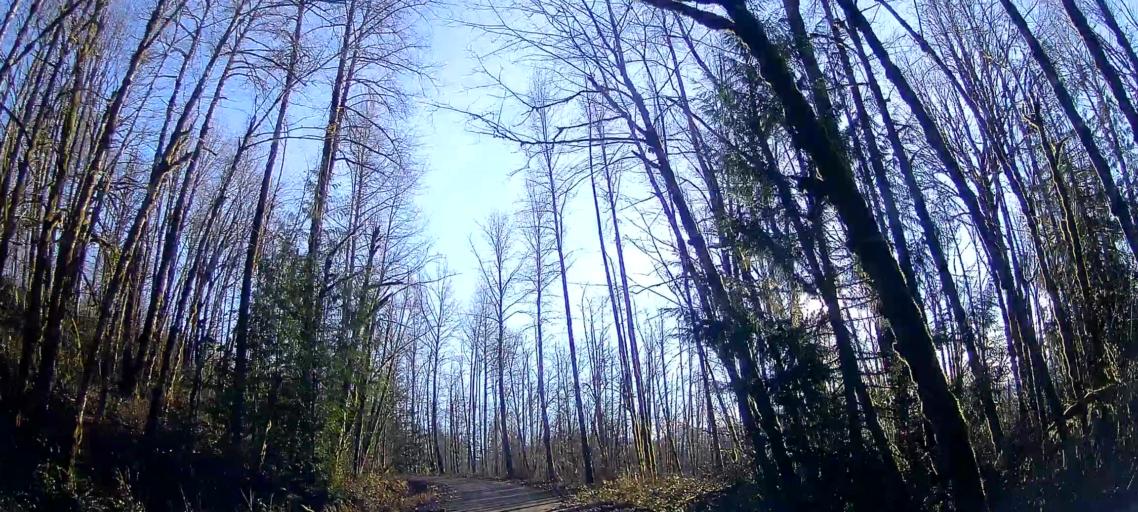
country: US
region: Washington
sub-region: Snohomish County
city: Darrington
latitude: 48.5463
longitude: -121.7391
